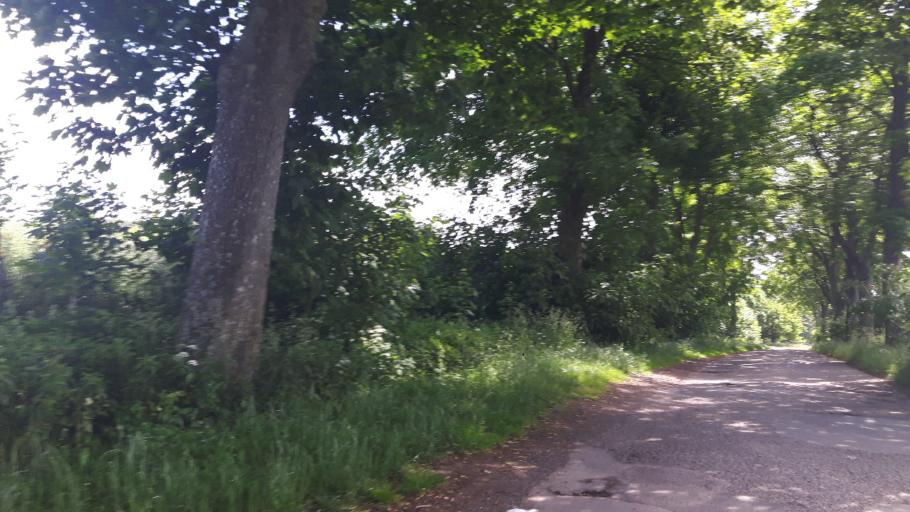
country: PL
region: West Pomeranian Voivodeship
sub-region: Powiat slawienski
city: Darlowo
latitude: 54.4651
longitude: 16.5012
